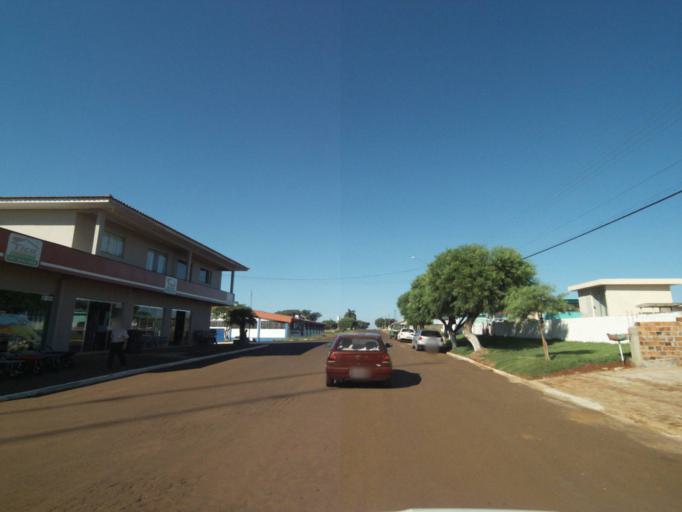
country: BR
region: Parana
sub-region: Laranjeiras Do Sul
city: Laranjeiras do Sul
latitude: -25.4918
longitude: -52.5304
